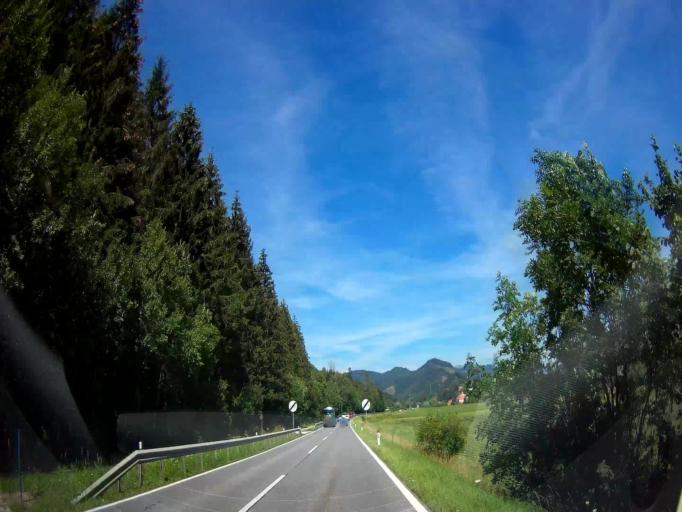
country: AT
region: Carinthia
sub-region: Politischer Bezirk Sankt Veit an der Glan
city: Althofen
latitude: 46.8811
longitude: 14.4478
